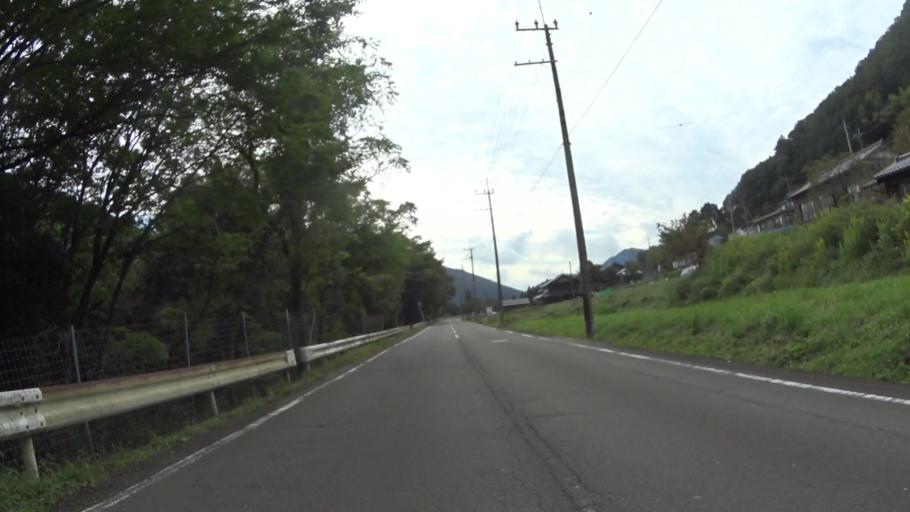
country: JP
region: Kyoto
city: Ayabe
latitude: 35.2611
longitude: 135.4291
